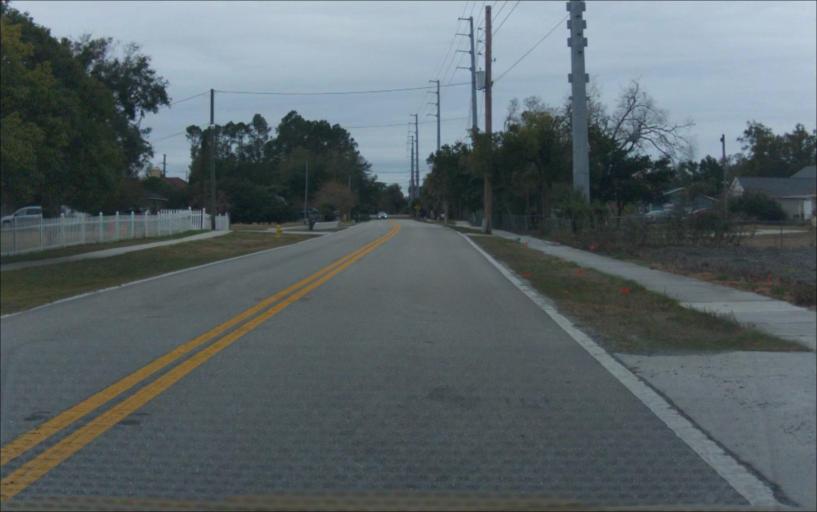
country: US
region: Florida
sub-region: Seminole County
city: Goldenrod
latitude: 28.6238
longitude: -81.2964
